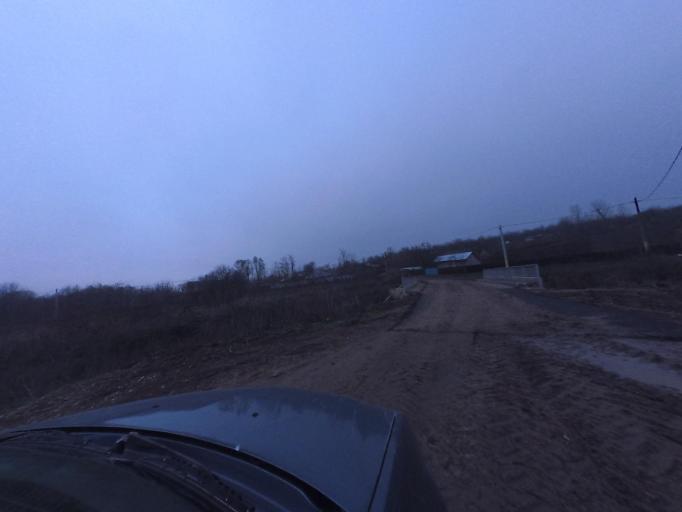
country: RO
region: Vaslui
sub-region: Comuna Vinderei
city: Vinderei
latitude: 46.1435
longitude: 27.7475
